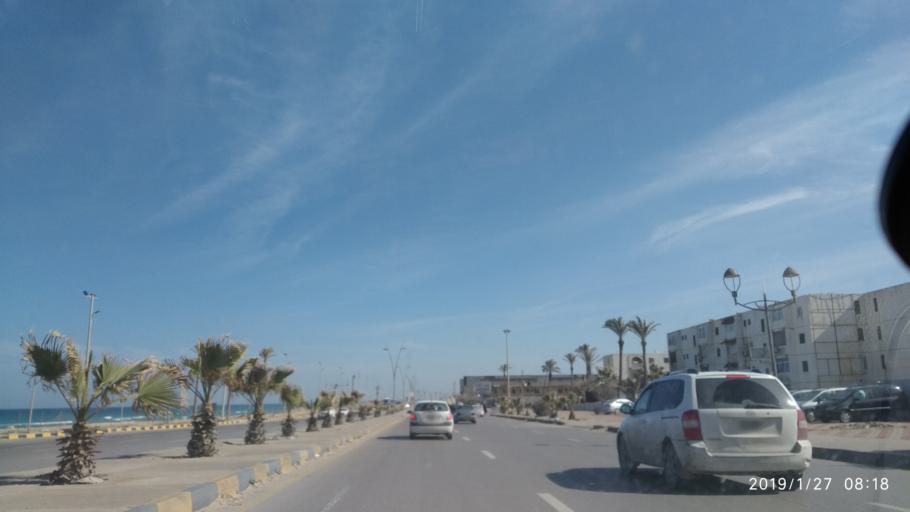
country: LY
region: Tripoli
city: Tagiura
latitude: 32.9075
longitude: 13.2696
